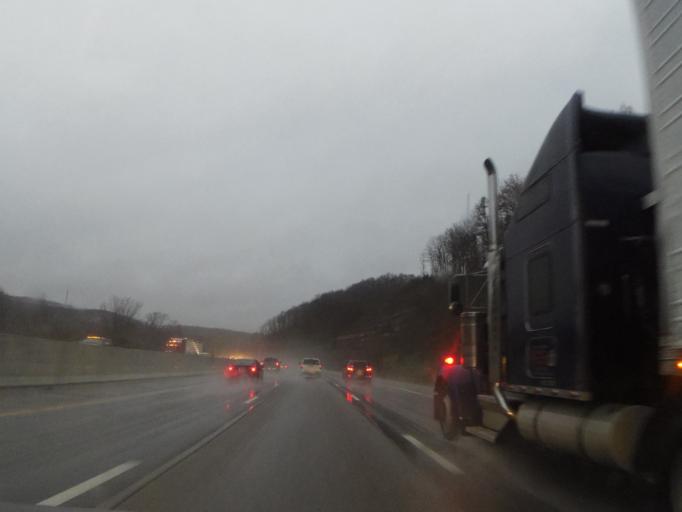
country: US
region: Kentucky
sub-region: Rockcastle County
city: Mount Vernon
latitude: 37.2462
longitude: -84.2455
